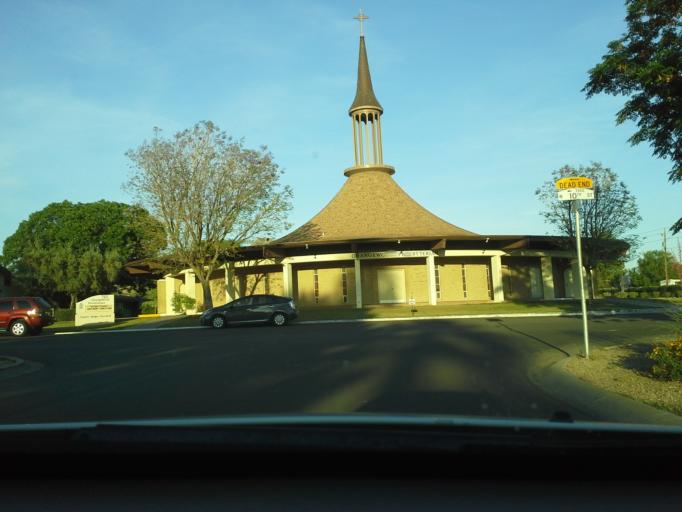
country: US
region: Arizona
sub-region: Maricopa County
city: Phoenix
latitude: 33.5441
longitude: -112.0610
